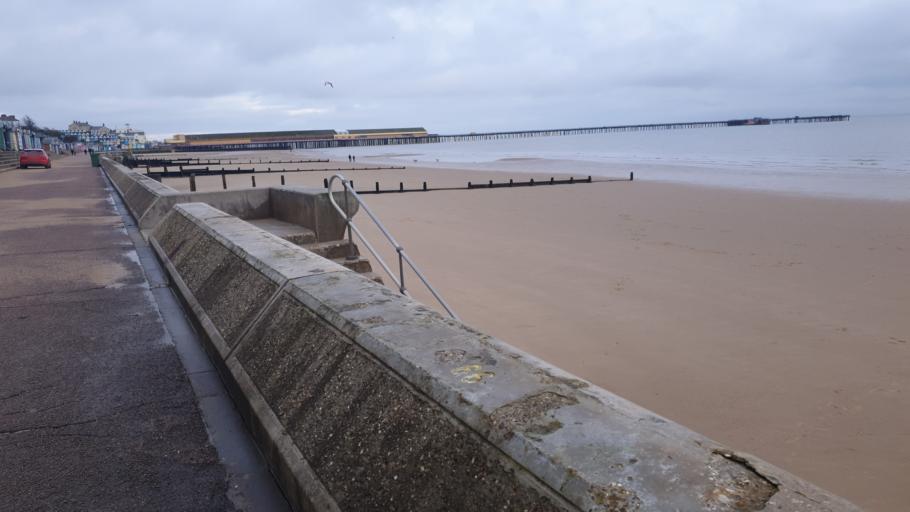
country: GB
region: England
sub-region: Essex
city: Walton-on-the-Naze
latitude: 51.8421
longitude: 1.2662
